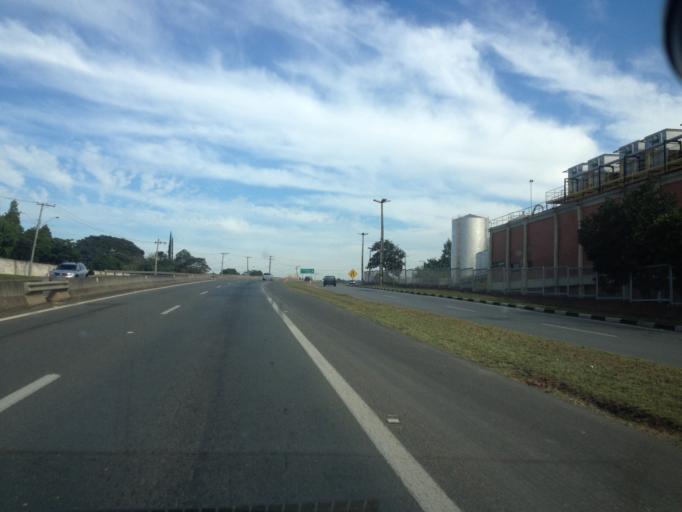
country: BR
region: Sao Paulo
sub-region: Itu
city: Itu
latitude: -23.2545
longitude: -47.3441
